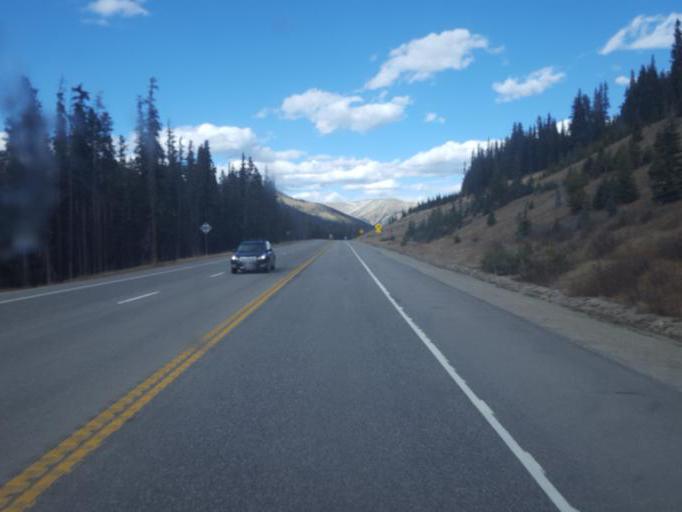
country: US
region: Colorado
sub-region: Summit County
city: Breckenridge
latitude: 39.4241
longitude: -106.1723
